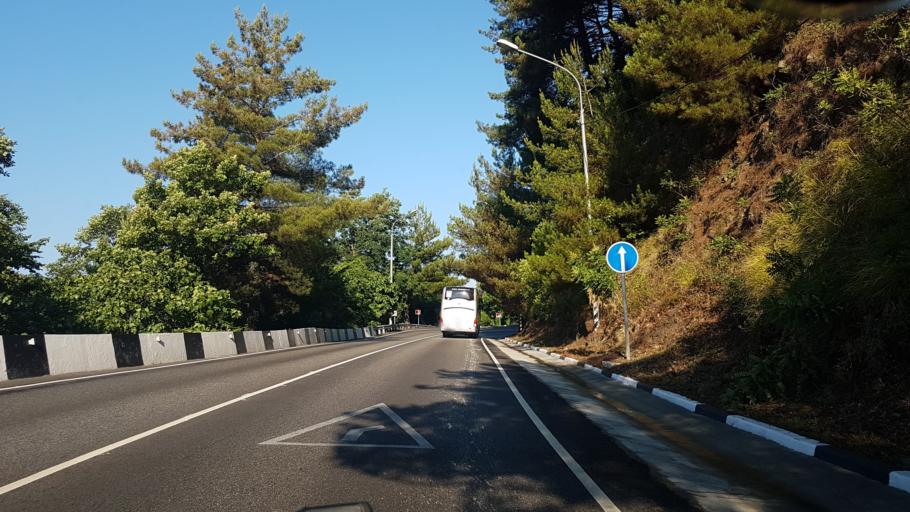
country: RU
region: Krasnodarskiy
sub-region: Sochi City
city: Lazarevskoye
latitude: 43.8384
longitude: 39.4188
